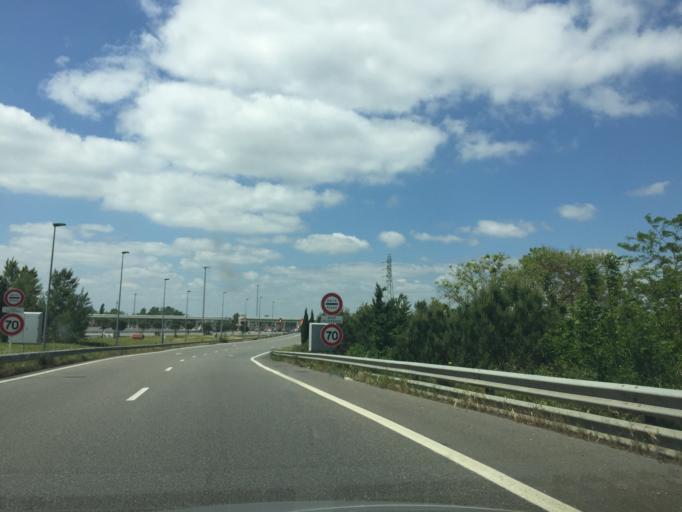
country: FR
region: Midi-Pyrenees
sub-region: Departement de la Haute-Garonne
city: Aucamville
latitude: 43.6557
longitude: 1.4298
